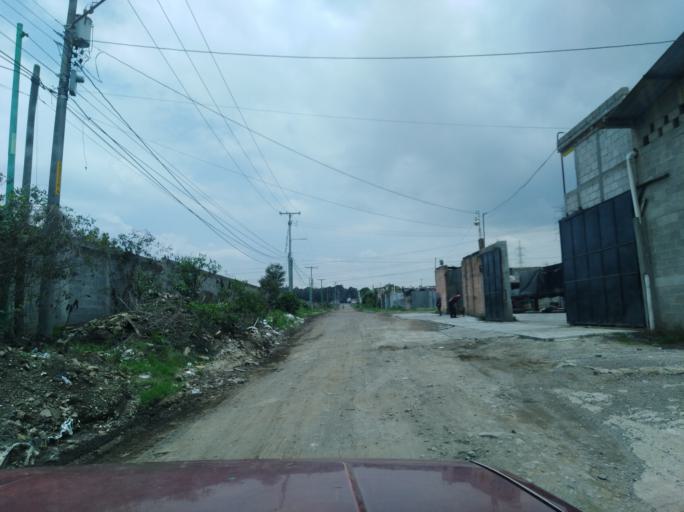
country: GT
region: Guatemala
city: Villa Nueva
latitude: 14.5248
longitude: -90.6195
